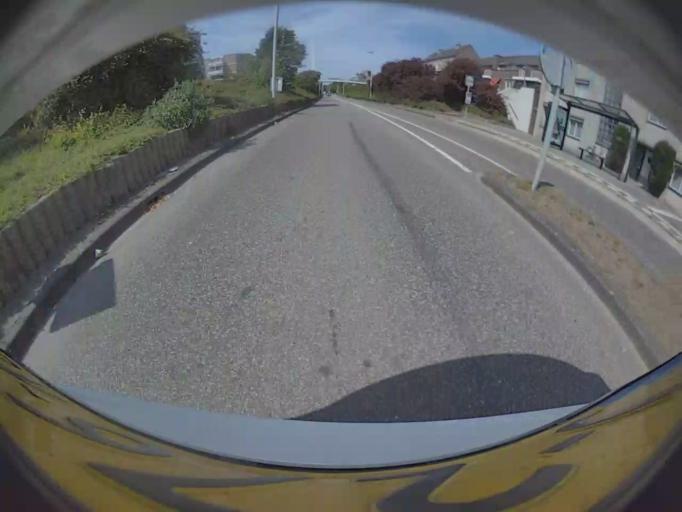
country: NL
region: South Holland
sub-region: Gemeente Voorschoten
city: Voorschoten
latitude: 52.1525
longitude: 4.4526
